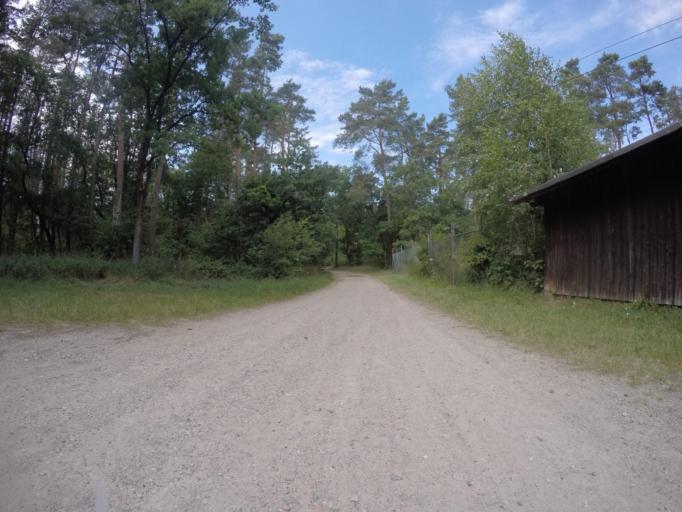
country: DE
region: Lower Saxony
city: Bleckede
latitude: 53.2773
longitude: 10.7363
